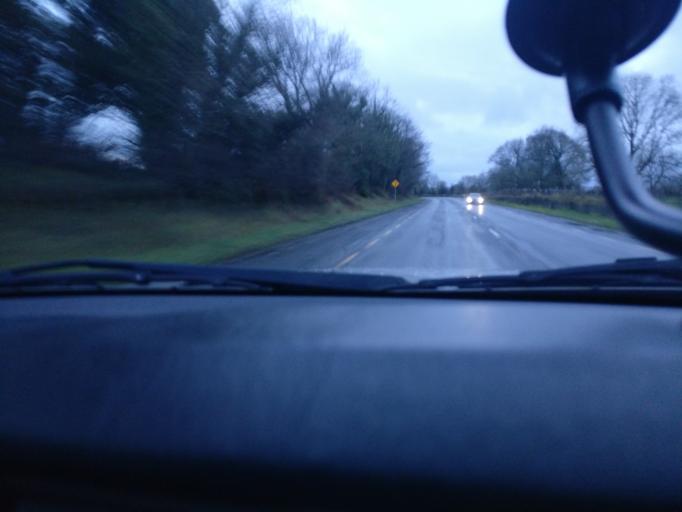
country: IE
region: Connaught
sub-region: County Galway
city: Loughrea
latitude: 53.2400
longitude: -8.4523
